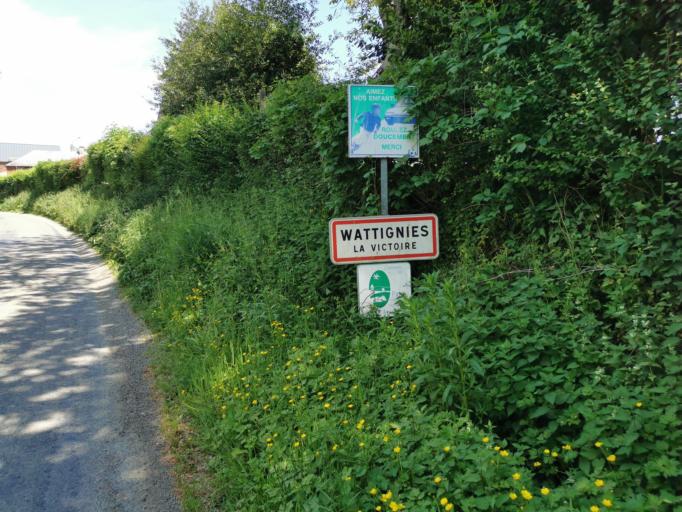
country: FR
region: Nord-Pas-de-Calais
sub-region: Departement du Nord
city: Ferriere-la-Grande
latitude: 50.2002
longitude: 4.0143
